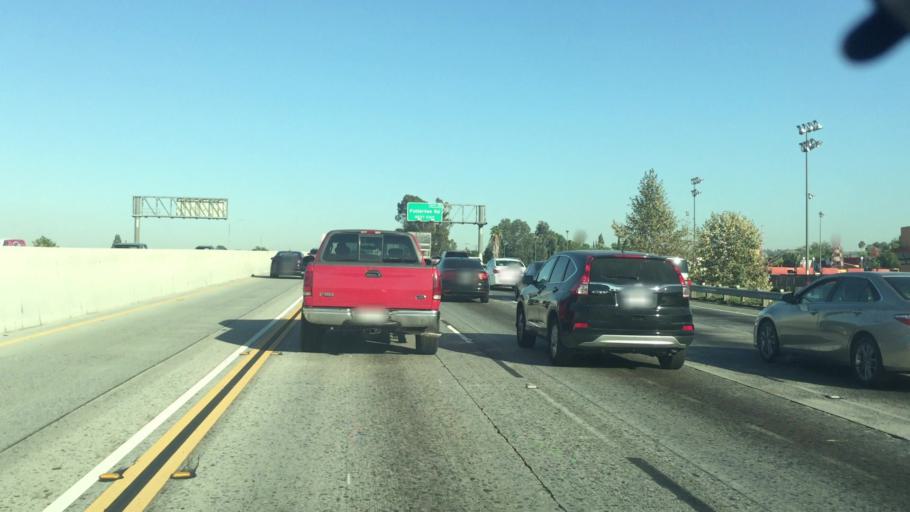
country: US
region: California
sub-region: Los Angeles County
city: South San Jose Hills
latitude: 33.9948
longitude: -117.9148
